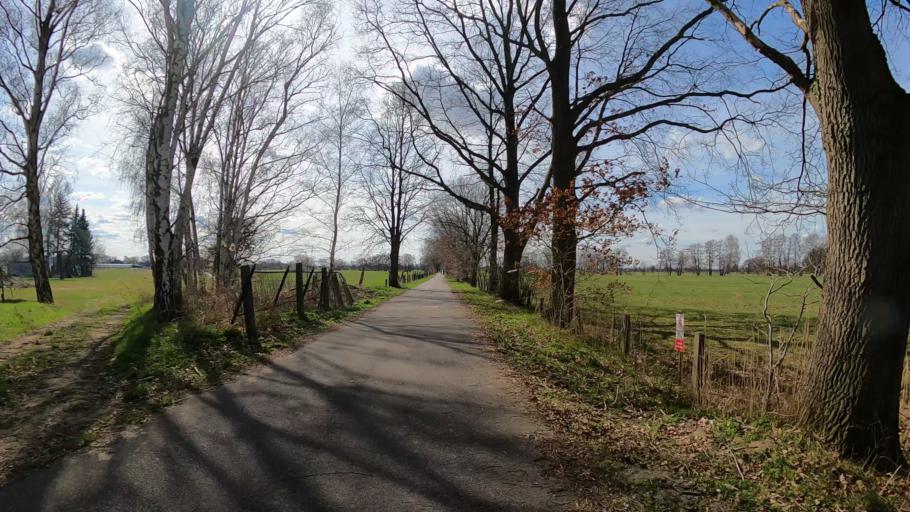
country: DE
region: Schleswig-Holstein
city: Escheburg
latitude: 53.4399
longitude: 10.2985
